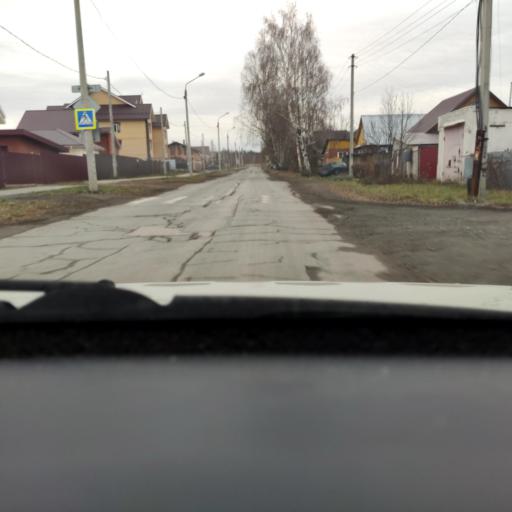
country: RU
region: Perm
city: Polazna
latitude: 58.1273
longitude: 56.4004
